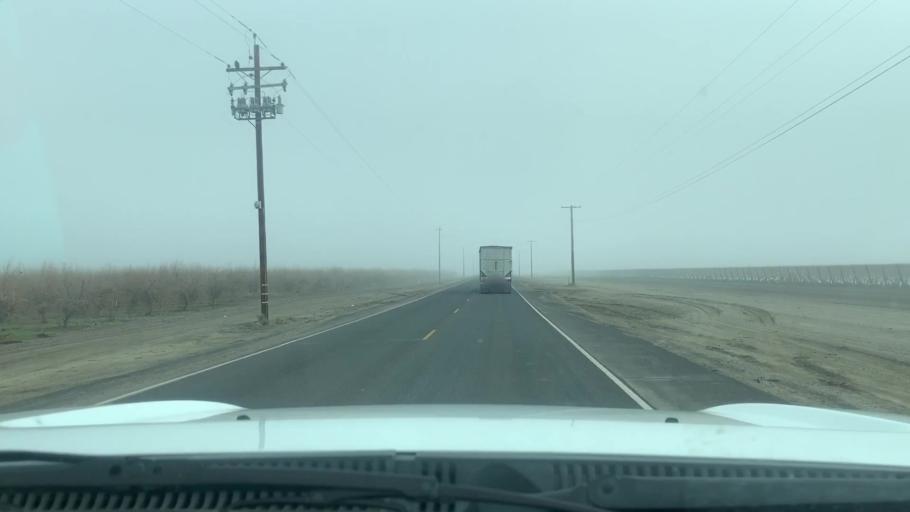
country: US
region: California
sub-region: Kern County
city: Lost Hills
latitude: 35.4995
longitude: -119.6139
